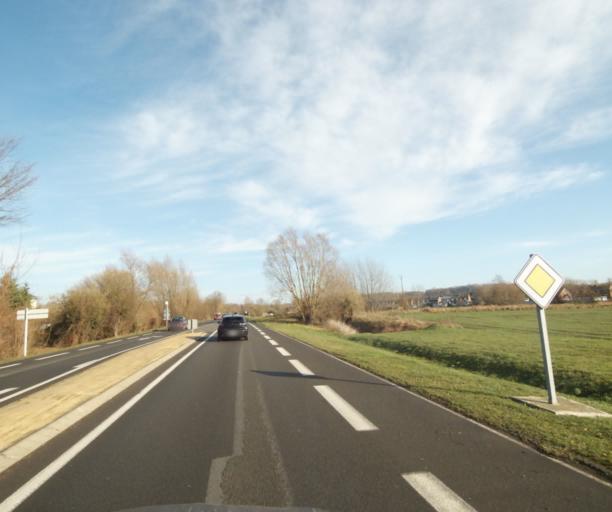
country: FR
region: Nord-Pas-de-Calais
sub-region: Departement du Nord
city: Trith-Saint-Leger
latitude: 50.3164
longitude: 3.4850
